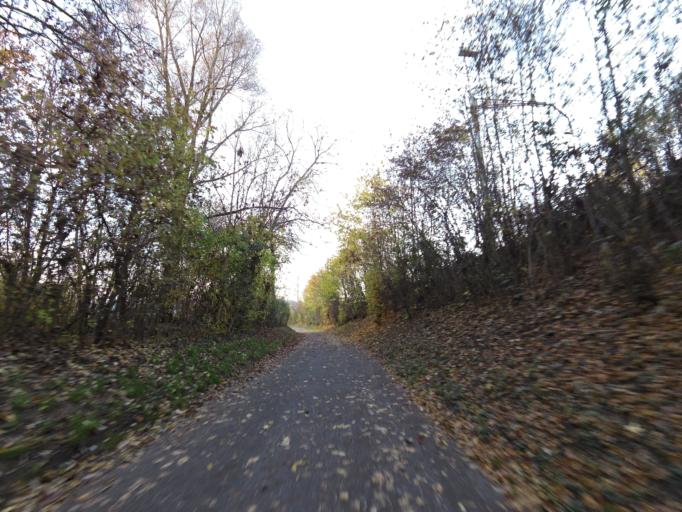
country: CH
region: Aargau
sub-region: Bezirk Aarau
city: Suhr
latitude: 47.3779
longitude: 8.0869
